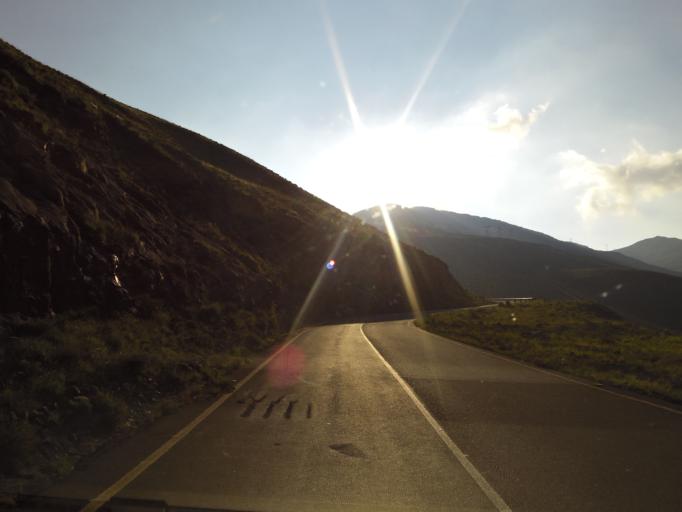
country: LS
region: Butha-Buthe
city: Butha-Buthe
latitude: -29.1123
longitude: 28.4494
